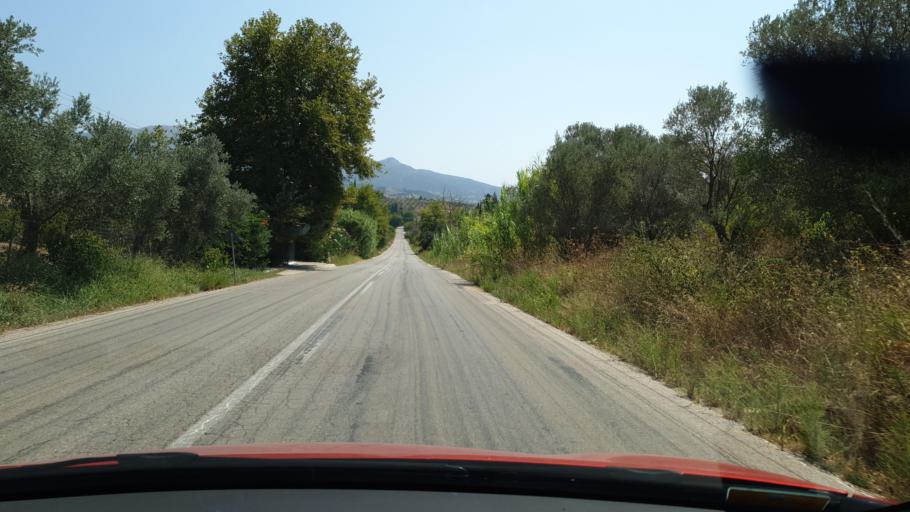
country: GR
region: Central Greece
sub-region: Nomos Evvoias
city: Oxilithos
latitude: 38.5205
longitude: 24.0960
